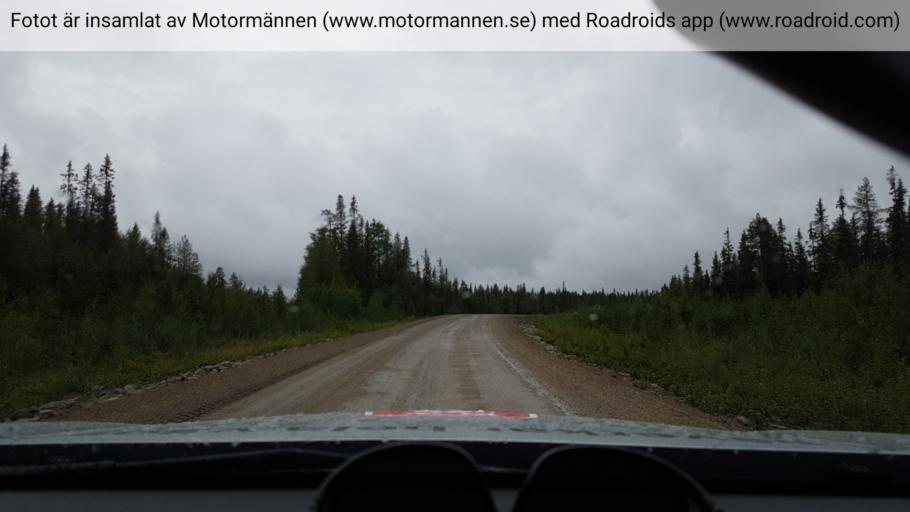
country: SE
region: Vaesterbotten
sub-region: Lycksele Kommun
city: Soderfors
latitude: 64.7875
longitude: 17.6531
